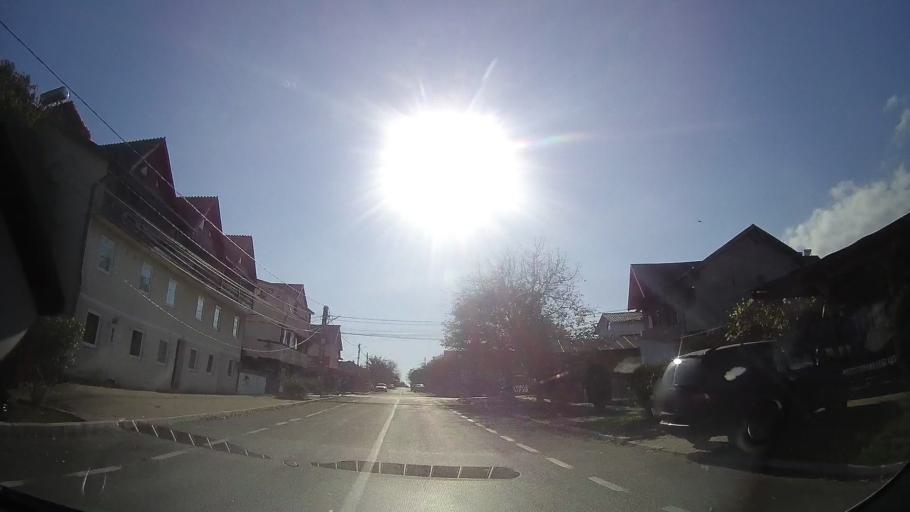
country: RO
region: Constanta
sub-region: Comuna Costinesti
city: Schitu
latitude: 43.9415
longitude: 28.6292
